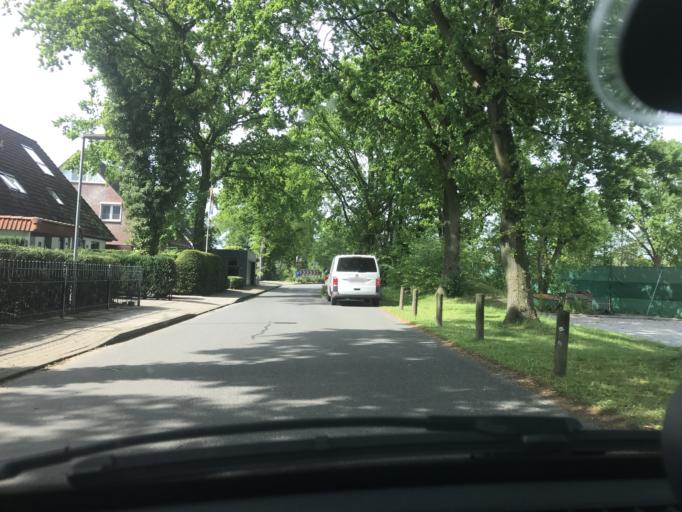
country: DE
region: Schleswig-Holstein
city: Witzhave
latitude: 53.5752
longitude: 10.3415
